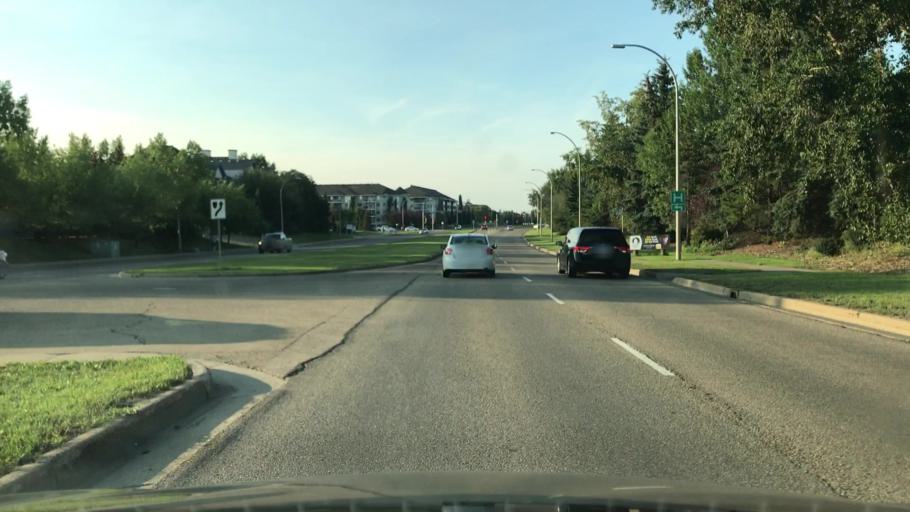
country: CA
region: Alberta
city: Edmonton
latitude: 53.4566
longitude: -113.4204
